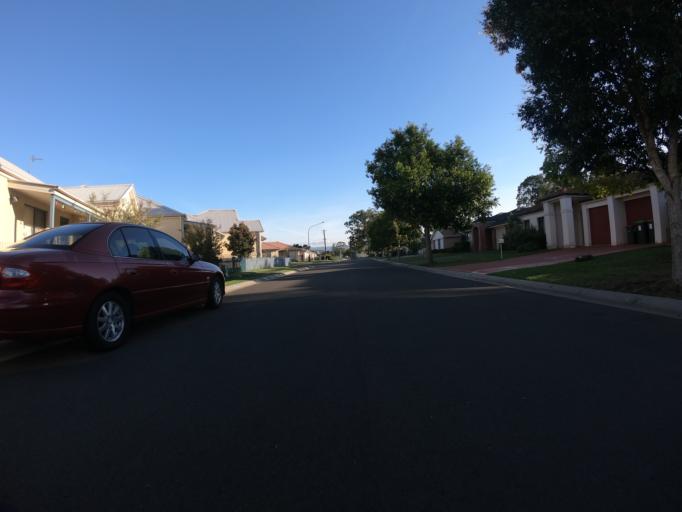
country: AU
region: New South Wales
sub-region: Wollongong
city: Dapto
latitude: -34.4888
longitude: 150.7957
